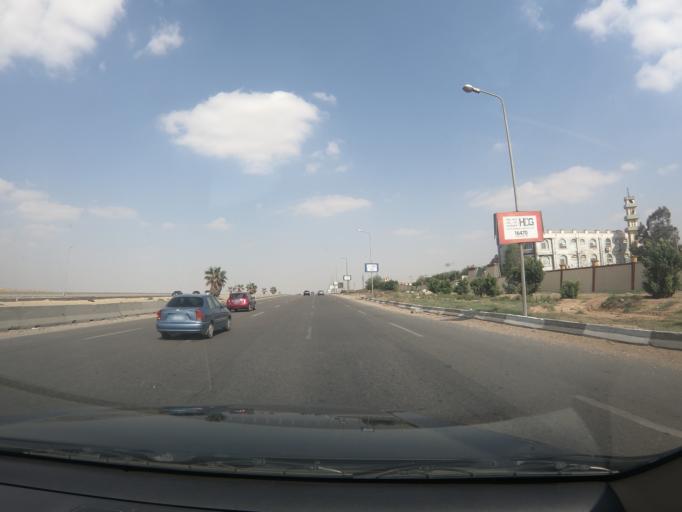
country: EG
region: Muhafazat al Qalyubiyah
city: Al Khankah
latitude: 30.0850
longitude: 31.4809
